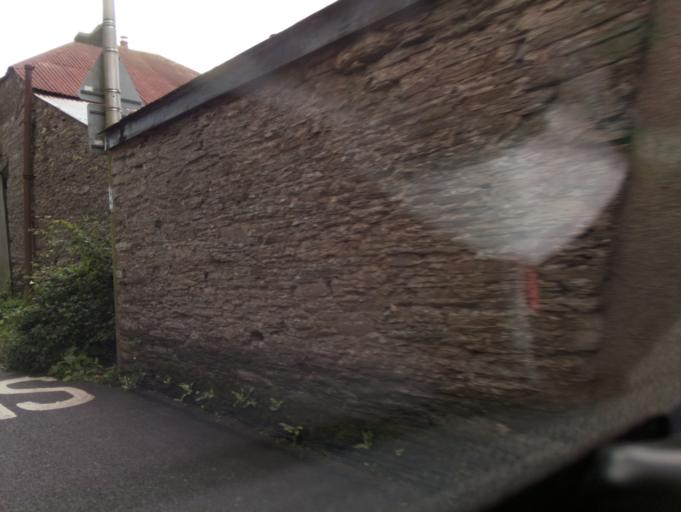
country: GB
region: England
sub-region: Devon
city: Salcombe
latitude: 50.2729
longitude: -3.6960
